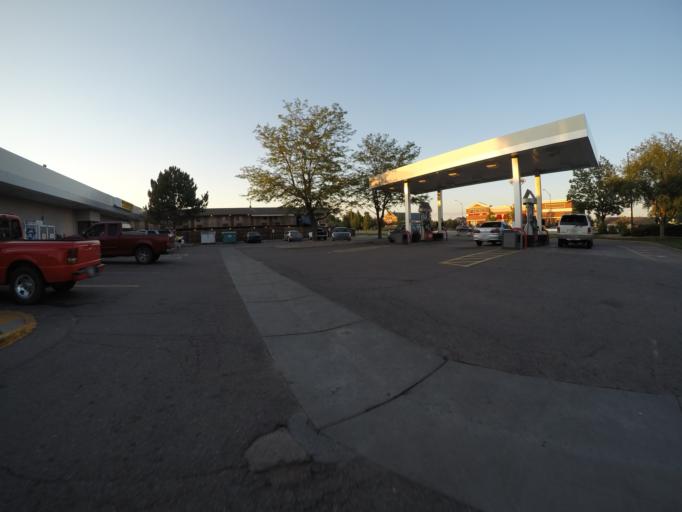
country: US
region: Colorado
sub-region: Larimer County
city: Fort Collins
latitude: 40.6109
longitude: -105.0771
